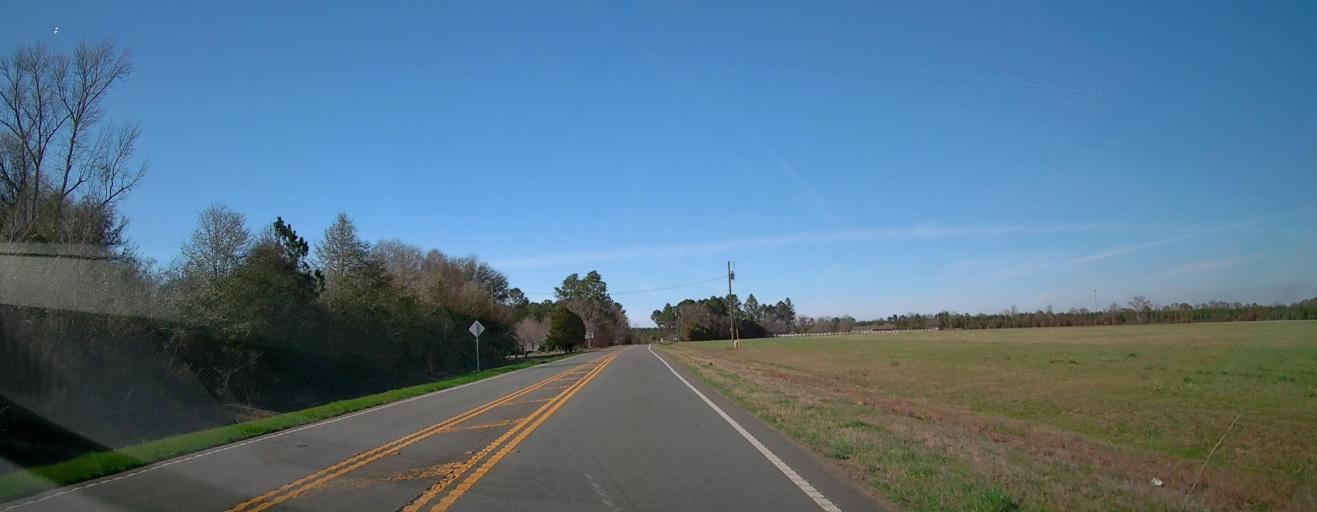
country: US
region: Georgia
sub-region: Macon County
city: Oglethorpe
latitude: 32.3228
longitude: -84.0692
